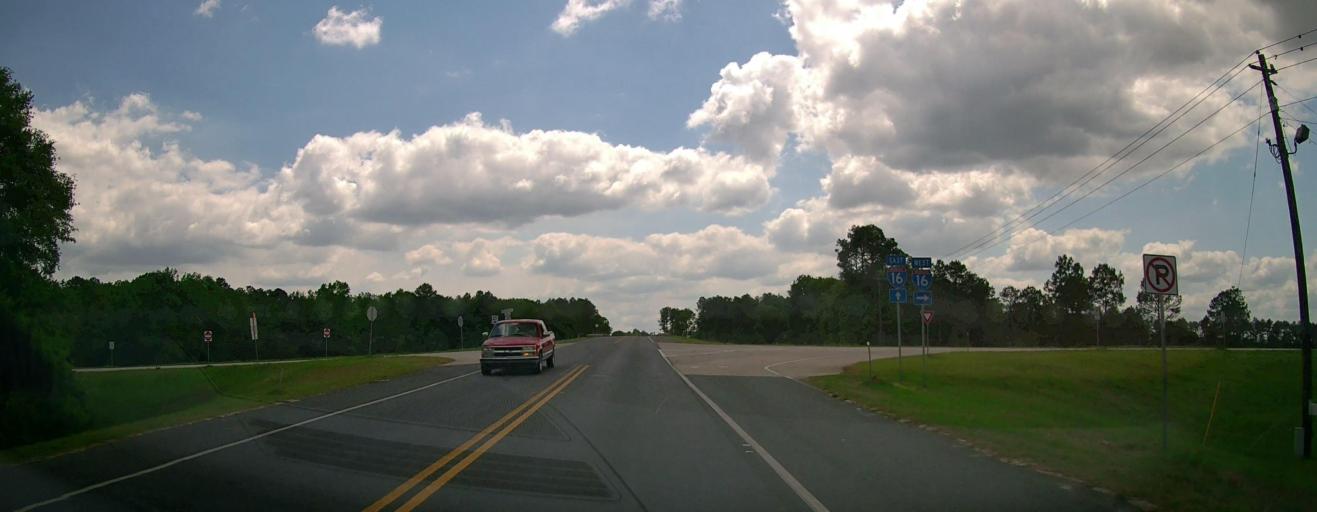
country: US
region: Georgia
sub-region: Treutlen County
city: Soperton
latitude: 32.4366
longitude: -82.6074
